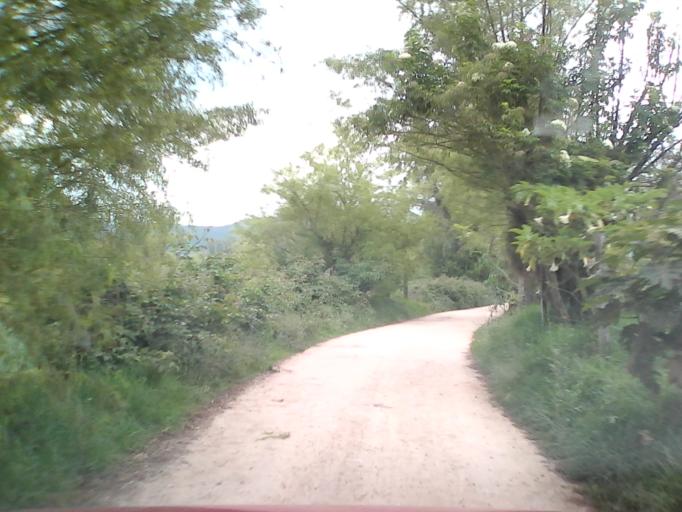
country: CO
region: Boyaca
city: Duitama
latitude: 5.8153
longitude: -73.0144
